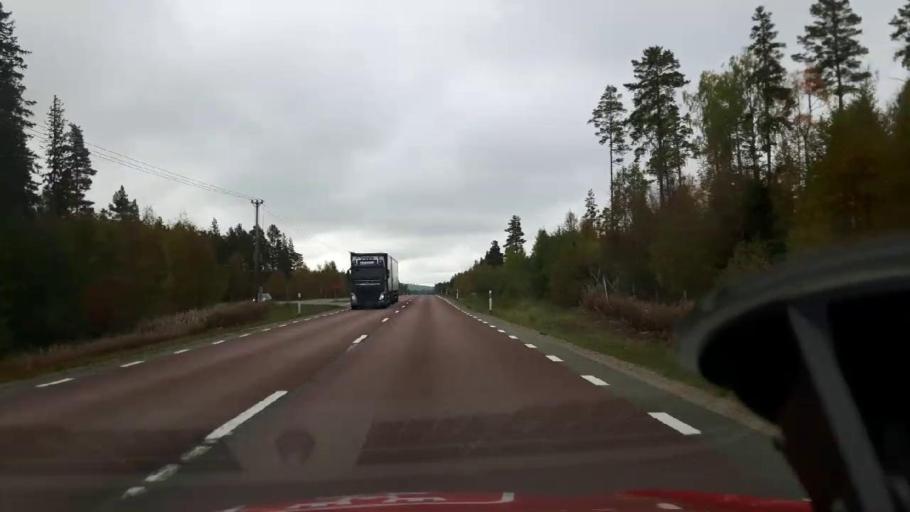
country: SE
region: Jaemtland
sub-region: Harjedalens Kommun
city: Sveg
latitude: 62.2409
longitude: 14.8302
